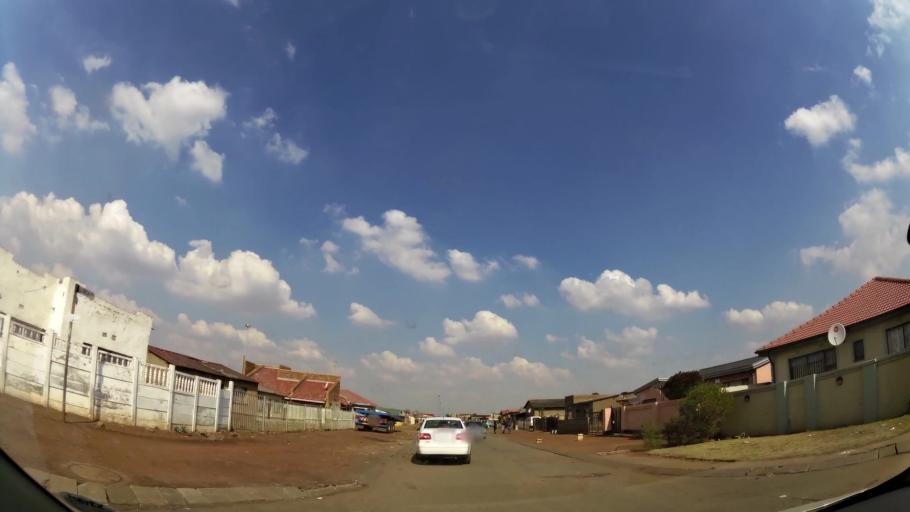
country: ZA
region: Gauteng
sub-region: Ekurhuleni Metropolitan Municipality
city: Germiston
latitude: -26.3378
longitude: 28.1446
